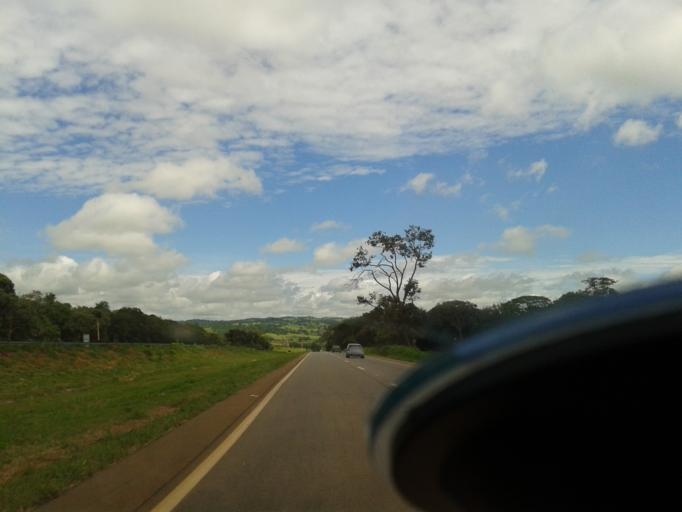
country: BR
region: Goias
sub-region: Inhumas
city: Inhumas
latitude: -16.2386
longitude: -49.5569
